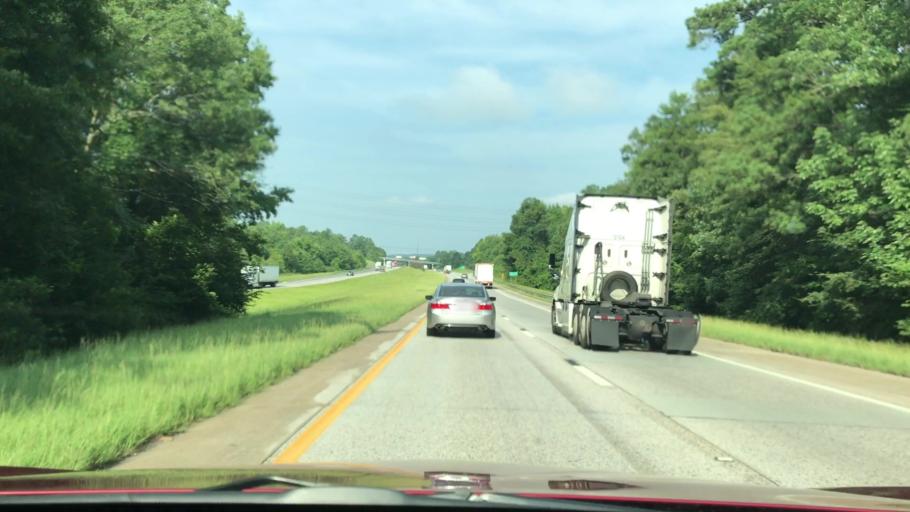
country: US
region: South Carolina
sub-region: Aiken County
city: Belvedere
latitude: 33.5427
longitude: -81.9829
